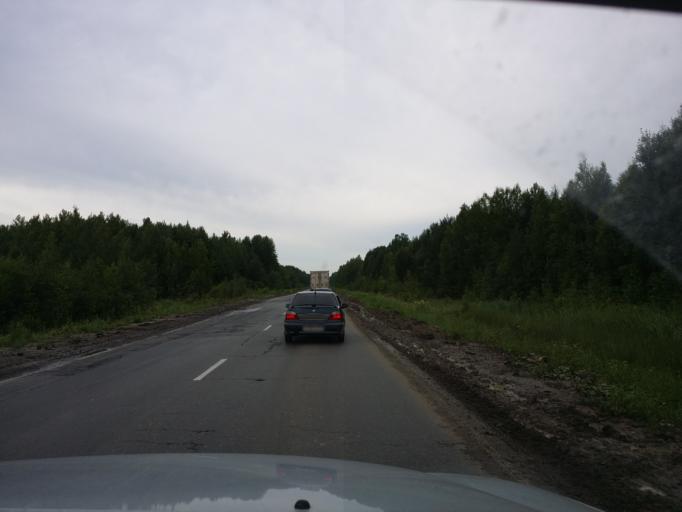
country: RU
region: Tjumen
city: Turtas
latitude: 58.6638
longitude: 68.8077
